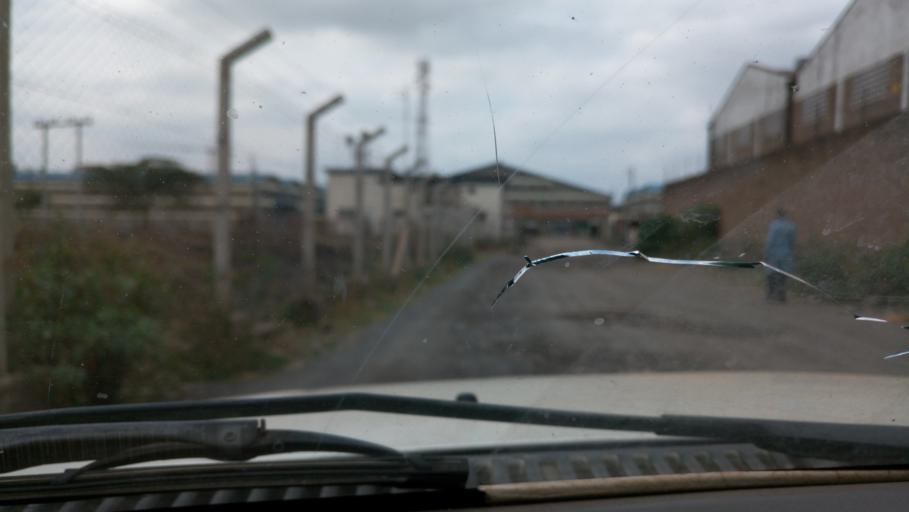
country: KE
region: Nairobi Area
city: Pumwani
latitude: -1.3229
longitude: 36.8655
